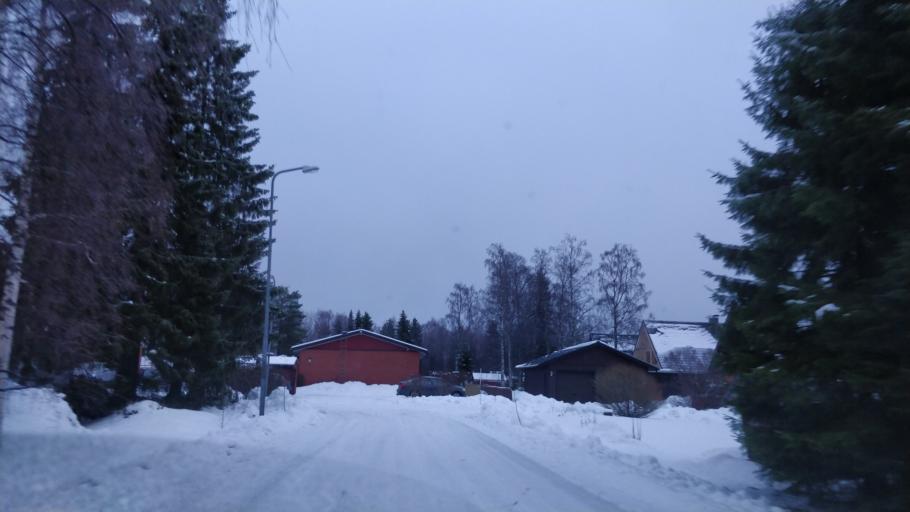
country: FI
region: Lapland
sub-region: Kemi-Tornio
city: Kemi
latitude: 65.7415
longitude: 24.6004
